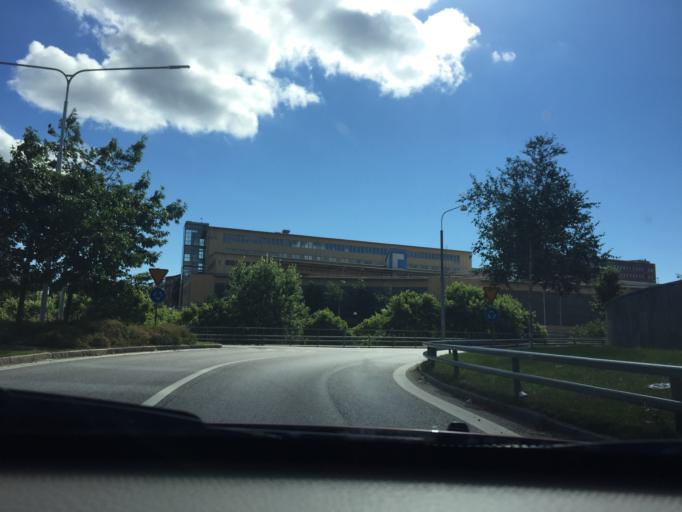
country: SE
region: Stockholm
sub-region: Stockholms Kommun
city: OEstermalm
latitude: 59.3046
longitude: 18.1140
